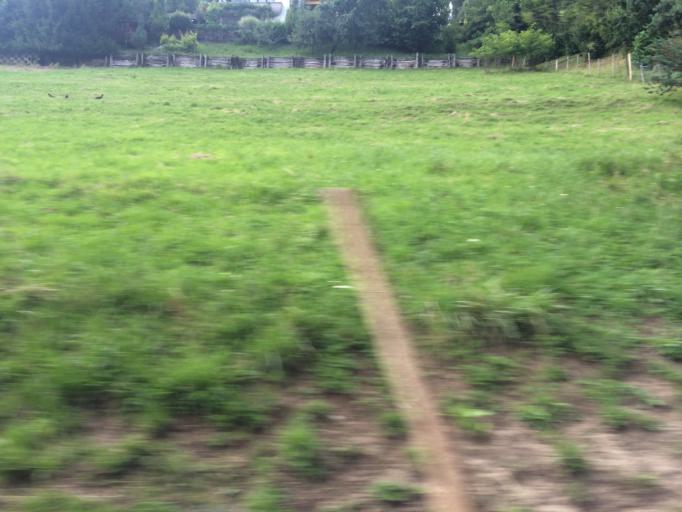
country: CH
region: Bern
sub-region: Bern-Mittelland District
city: Zollikofen
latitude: 46.9890
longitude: 7.4442
